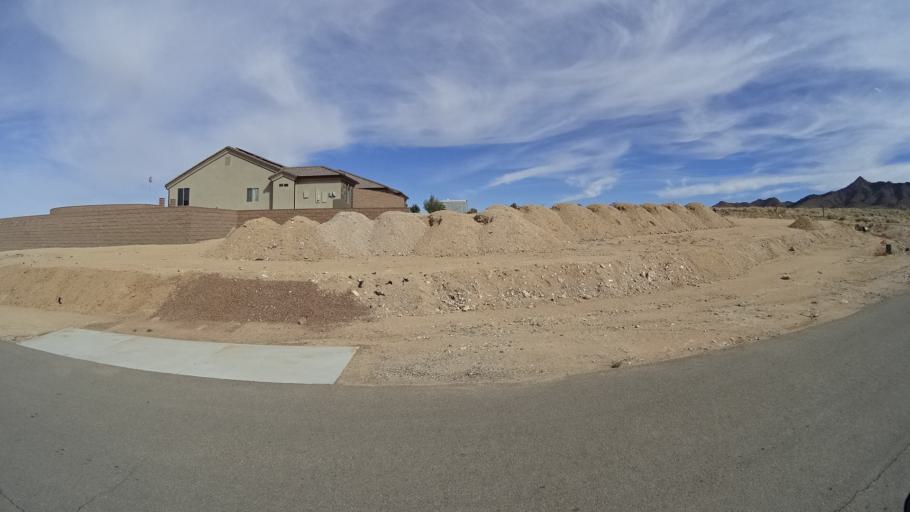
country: US
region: Arizona
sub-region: Mohave County
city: Kingman
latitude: 35.1863
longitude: -113.9769
